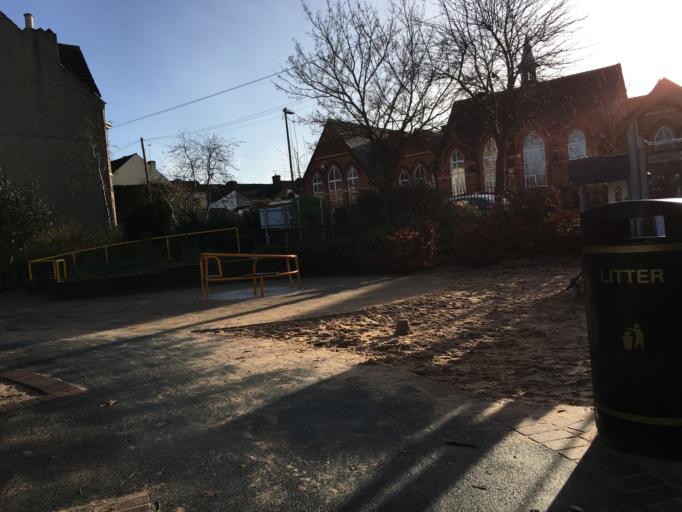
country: GB
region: England
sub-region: Warwickshire
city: Rugby
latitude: 52.3764
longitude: -1.2493
